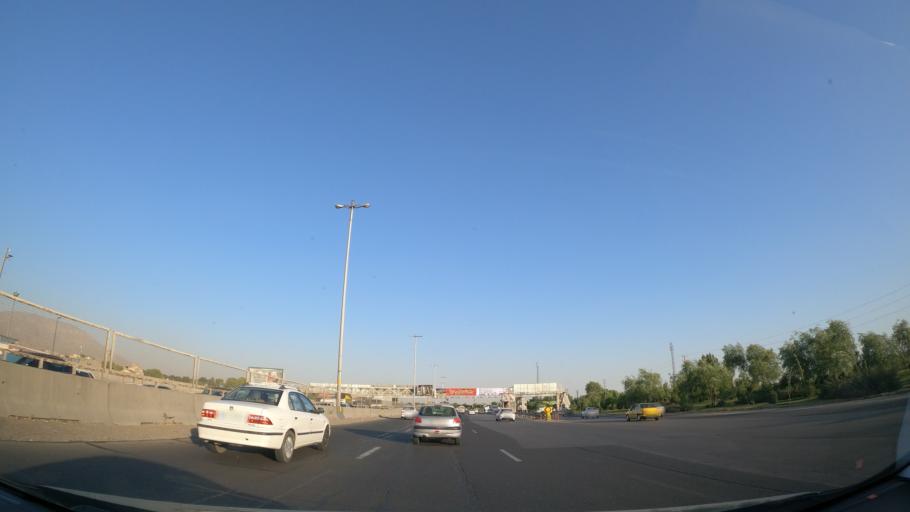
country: IR
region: Alborz
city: Karaj
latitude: 35.8038
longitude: 50.9682
